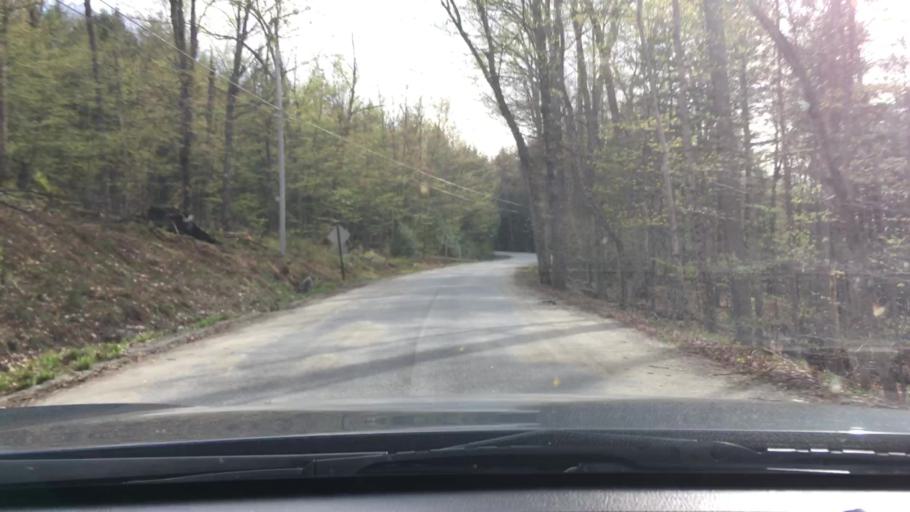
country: US
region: New York
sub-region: Essex County
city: Ticonderoga
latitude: 43.8175
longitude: -73.7425
